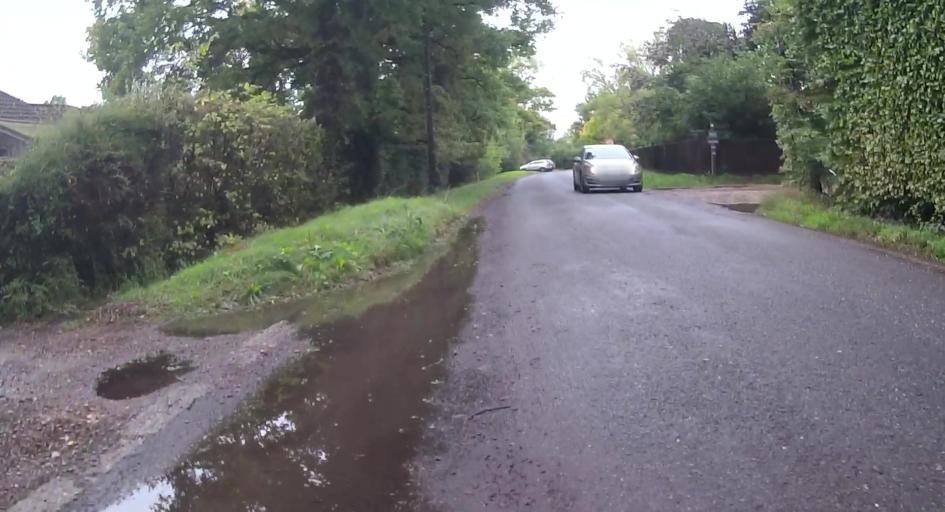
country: GB
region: England
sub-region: Hampshire
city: Tadley
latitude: 51.3318
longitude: -1.1638
